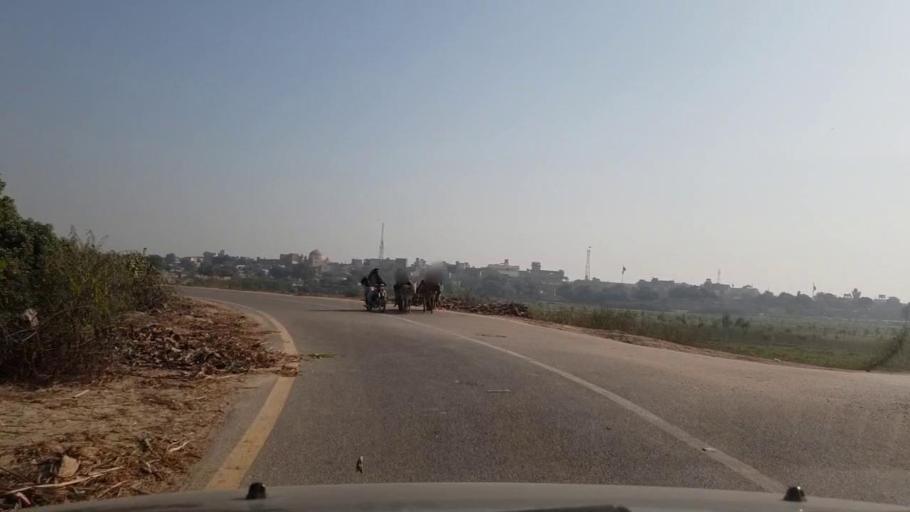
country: PK
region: Sindh
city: Tando Jam
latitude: 25.5175
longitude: 68.6111
